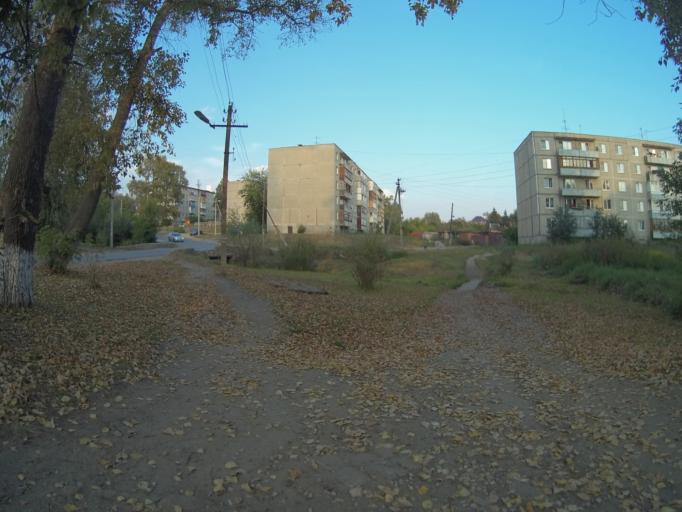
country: RU
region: Vladimir
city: Orgtrud
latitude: 56.1804
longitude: 40.6081
